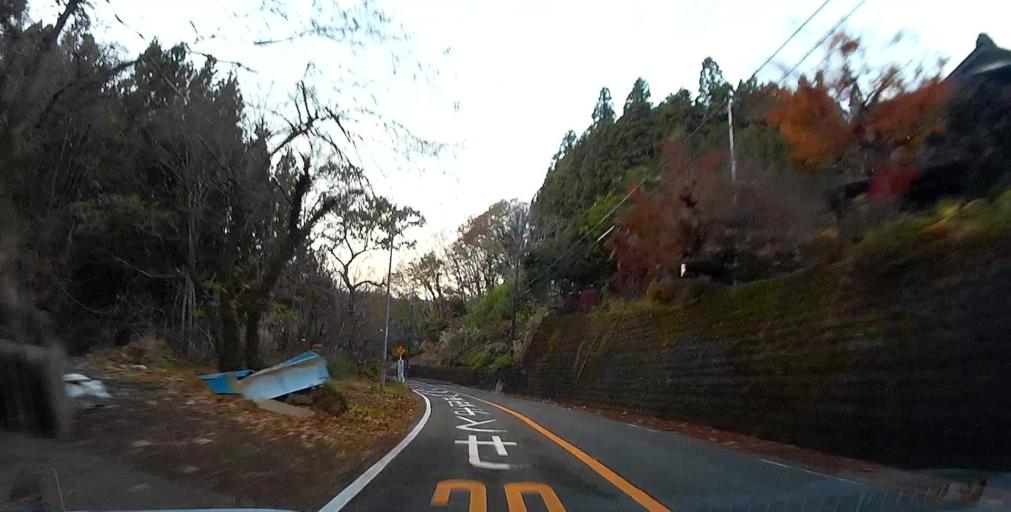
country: JP
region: Yamanashi
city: Uenohara
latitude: 35.5837
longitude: 139.1760
